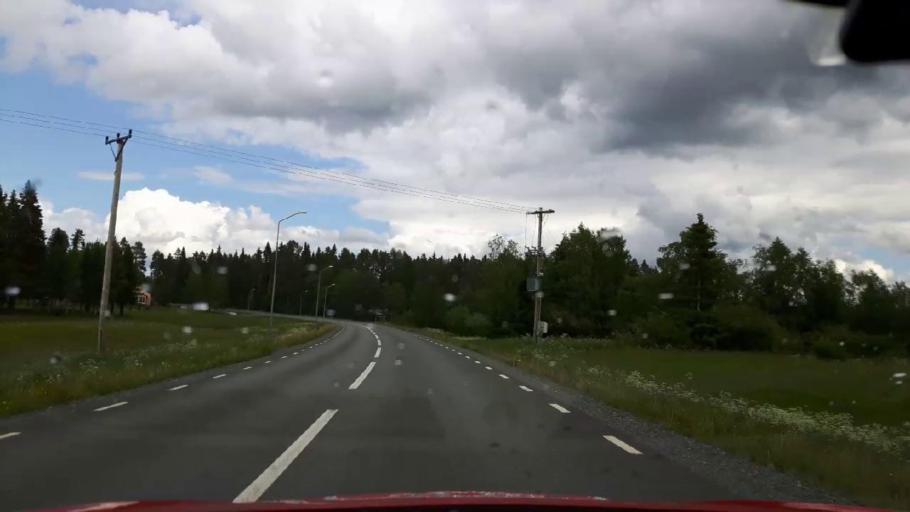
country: SE
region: Jaemtland
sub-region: Krokoms Kommun
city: Krokom
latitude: 63.5697
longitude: 14.2794
